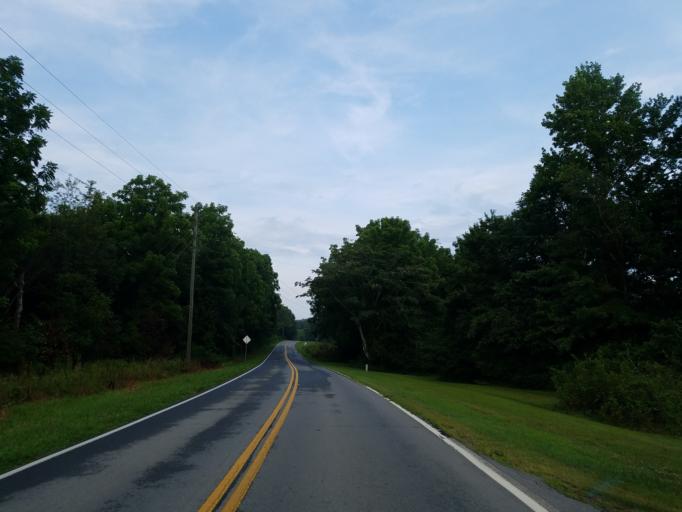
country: US
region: Georgia
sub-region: Pickens County
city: Jasper
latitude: 34.4573
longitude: -84.5406
